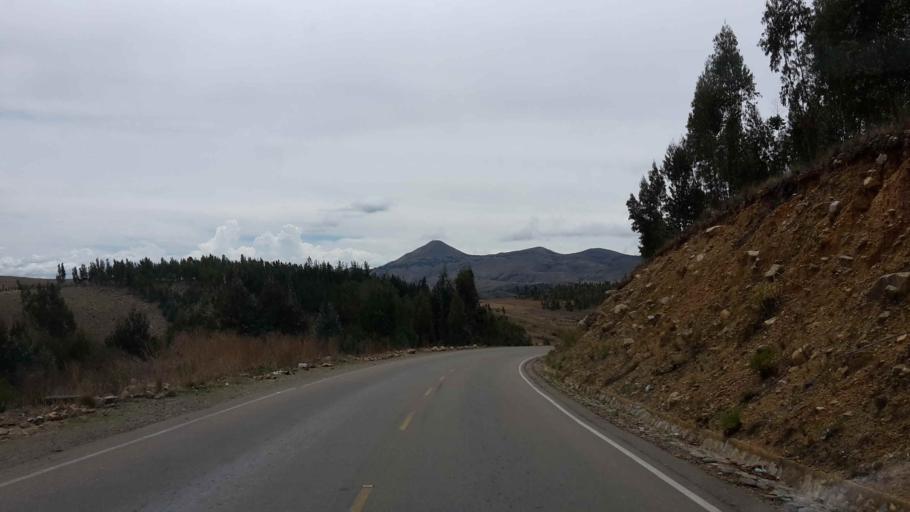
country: BO
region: Cochabamba
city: Arani
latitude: -17.4605
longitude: -65.7056
